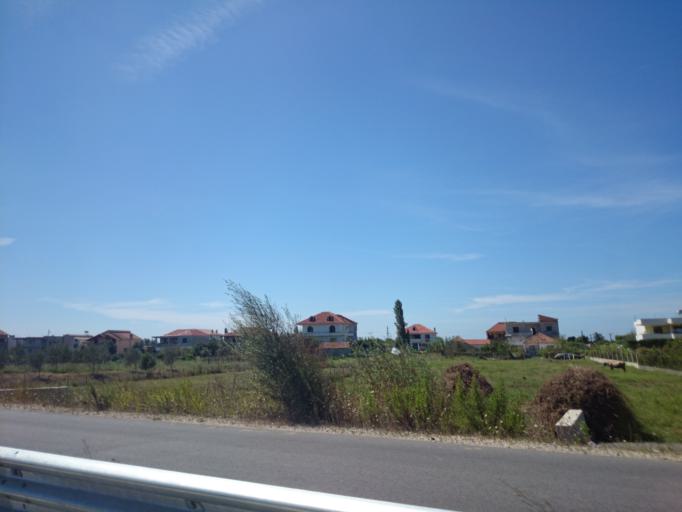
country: AL
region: Tirane
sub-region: Rrethi i Kavajes
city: Golem
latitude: 41.2180
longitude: 19.5298
